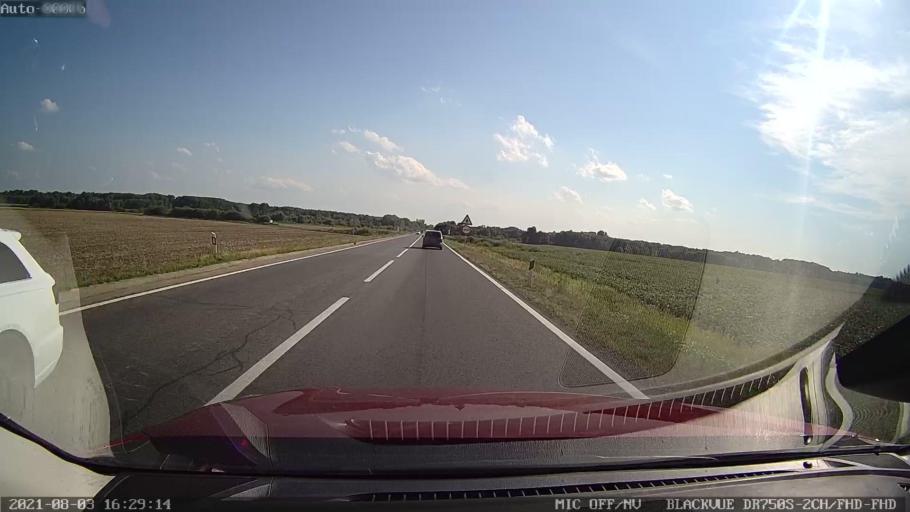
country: HR
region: Osjecko-Baranjska
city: Darda
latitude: 45.5994
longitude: 18.6569
